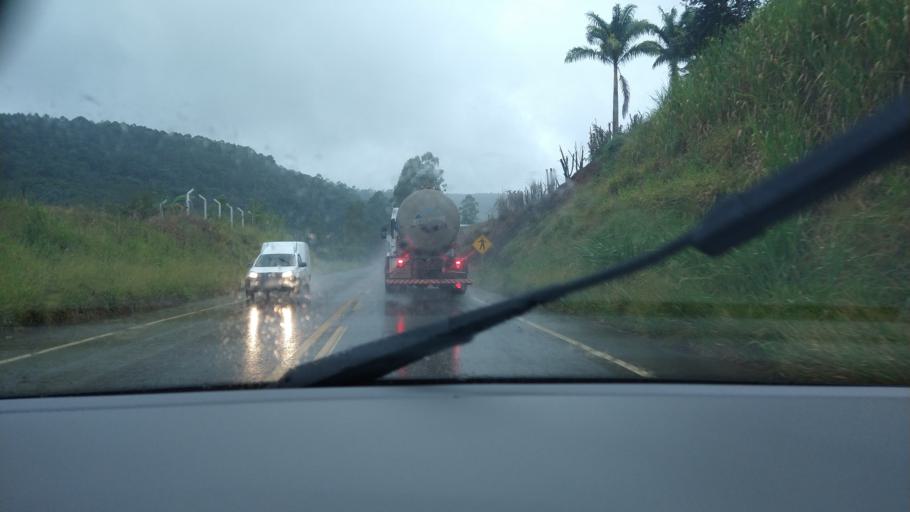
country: BR
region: Minas Gerais
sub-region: Vicosa
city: Vicosa
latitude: -20.5906
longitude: -42.8810
